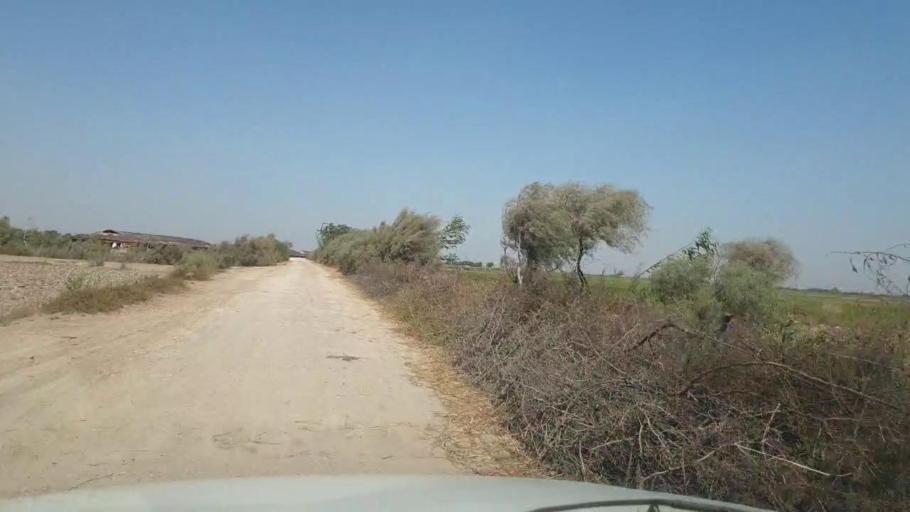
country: PK
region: Sindh
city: Chuhar Jamali
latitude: 24.3765
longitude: 67.8021
